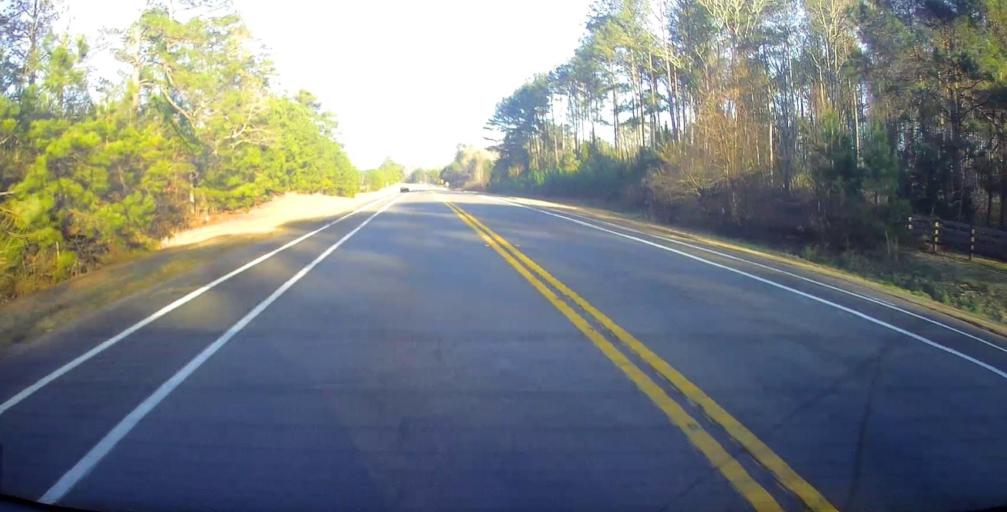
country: US
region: Georgia
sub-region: Harris County
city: Pine Mountain
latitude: 32.8505
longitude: -84.8775
